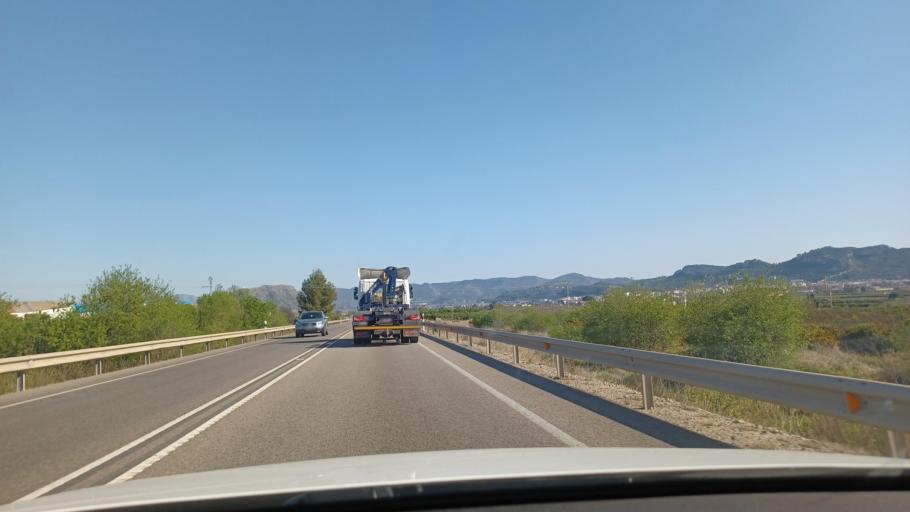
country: ES
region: Valencia
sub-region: Provincia de Valencia
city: Llosa de Ranes
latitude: 39.0159
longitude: -0.5470
